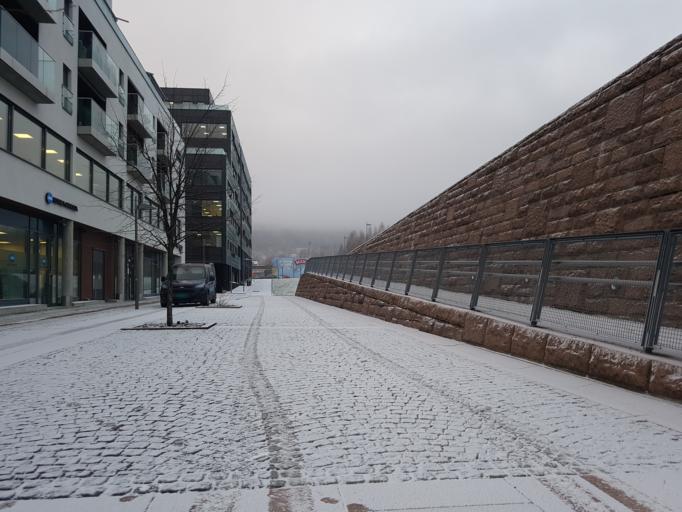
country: NO
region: Buskerud
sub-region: Drammen
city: Drammen
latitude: 59.7447
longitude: 10.1906
